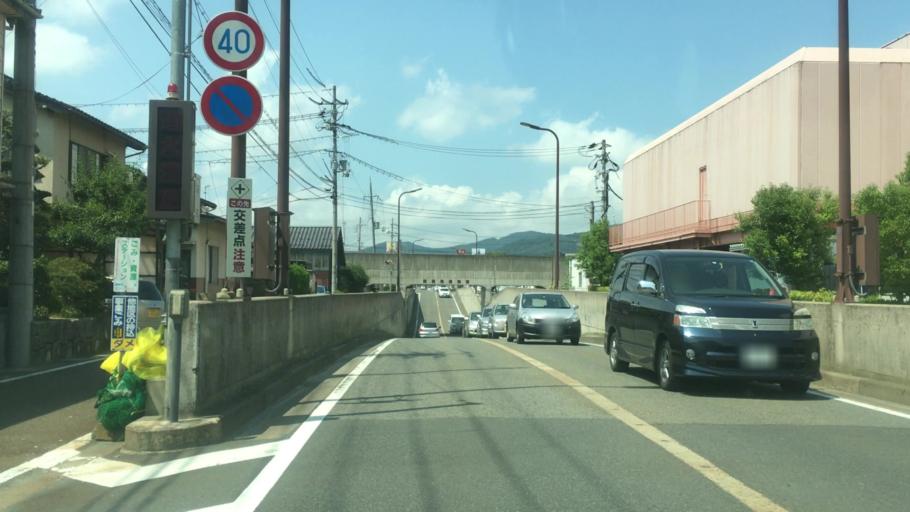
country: JP
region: Hyogo
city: Toyooka
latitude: 35.5506
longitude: 134.8155
